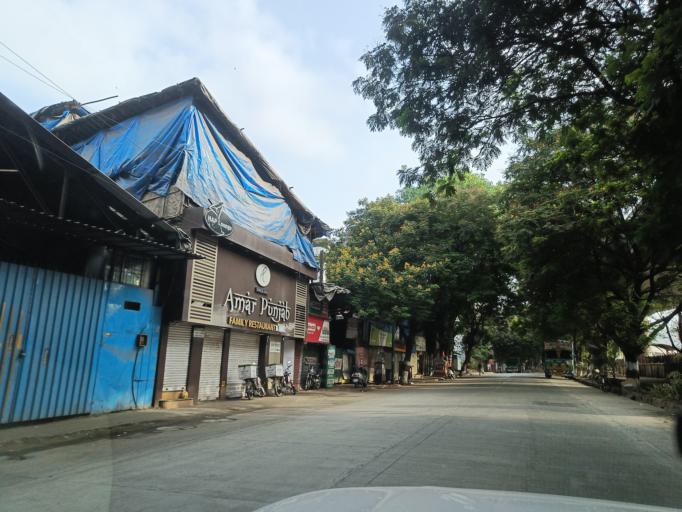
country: IN
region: Maharashtra
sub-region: Thane
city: Thane
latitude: 19.1961
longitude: 72.9621
